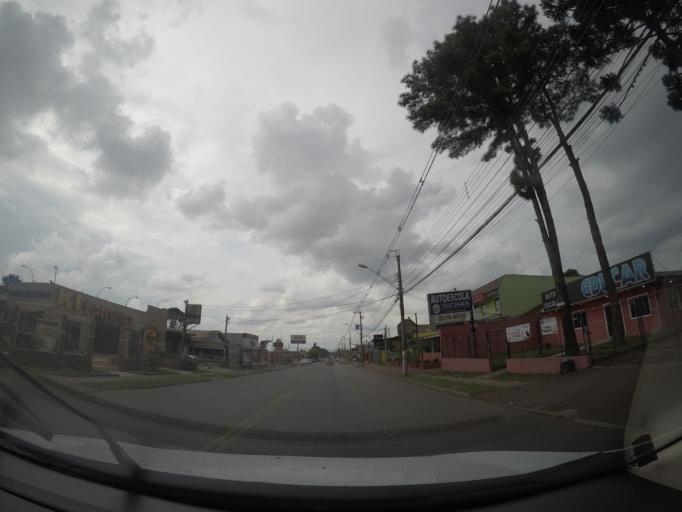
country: BR
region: Parana
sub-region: Sao Jose Dos Pinhais
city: Sao Jose dos Pinhais
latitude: -25.5196
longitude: -49.2341
